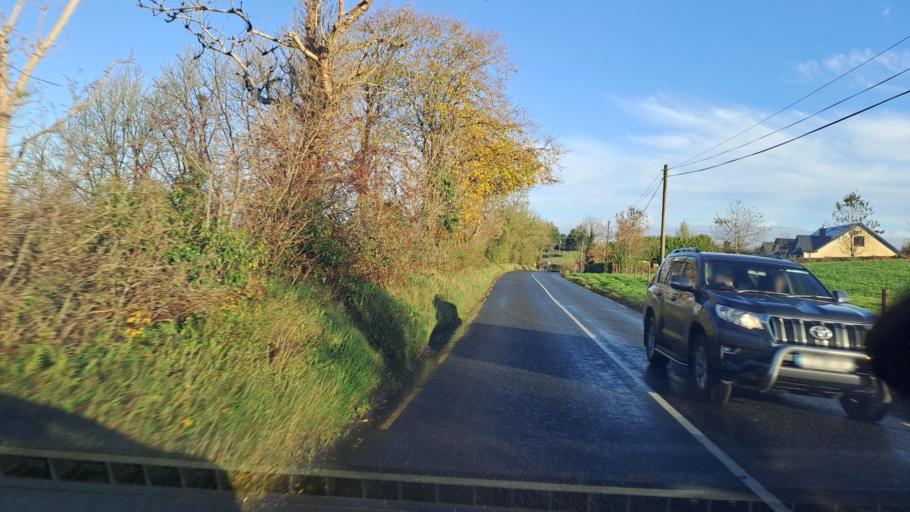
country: IE
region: Ulster
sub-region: County Monaghan
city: Monaghan
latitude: 54.2040
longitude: -6.9863
